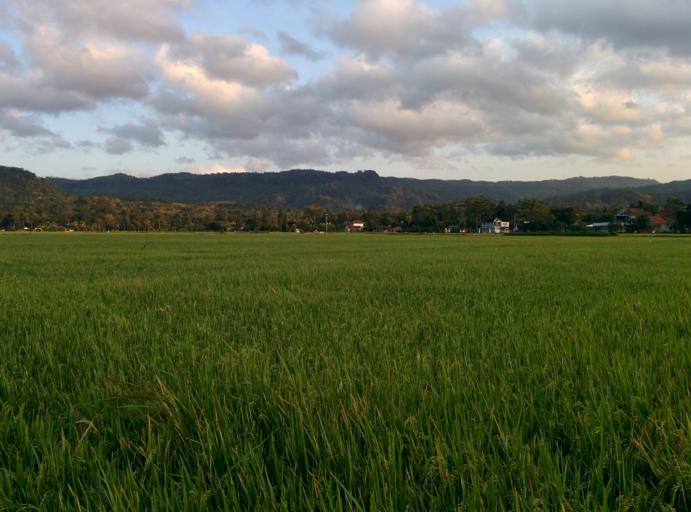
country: ID
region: East Java
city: Sitiarjo
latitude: -8.3817
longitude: 112.6792
